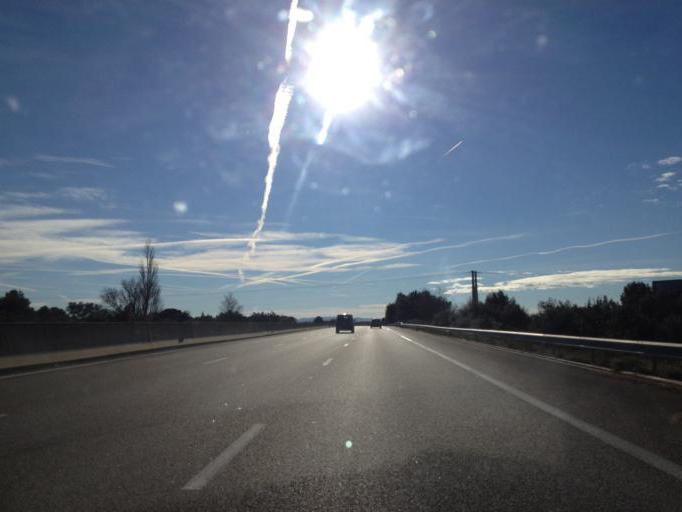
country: FR
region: Provence-Alpes-Cote d'Azur
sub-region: Departement du Vaucluse
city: Sorgues
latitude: 44.0101
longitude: 4.8901
